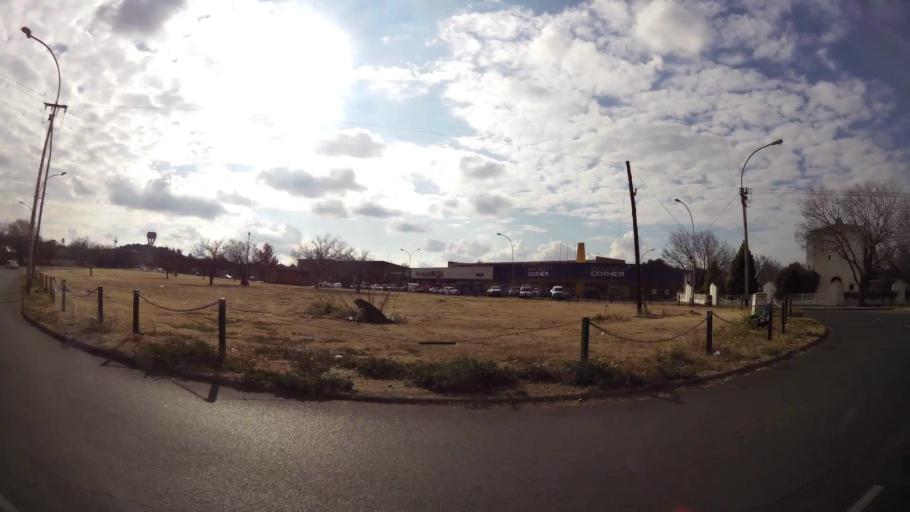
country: ZA
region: Orange Free State
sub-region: Mangaung Metropolitan Municipality
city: Bloemfontein
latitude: -29.0828
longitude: 26.2148
